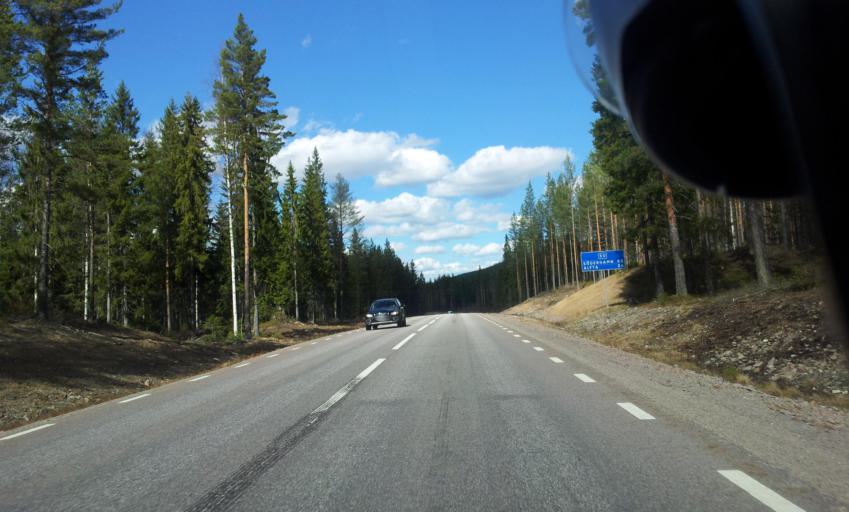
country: SE
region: Gaevleborg
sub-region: Ovanakers Kommun
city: Edsbyn
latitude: 61.1693
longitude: 15.8831
